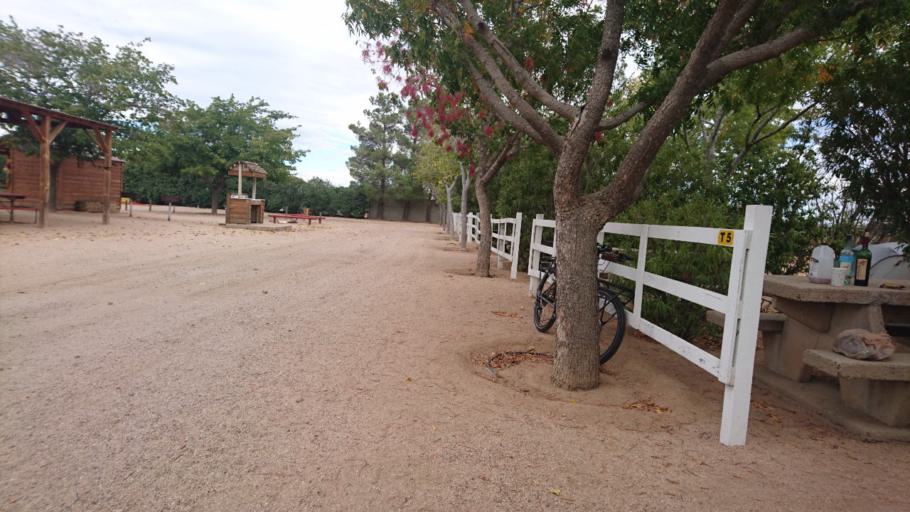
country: US
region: Arizona
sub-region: Mohave County
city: New Kingman-Butler
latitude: 35.2352
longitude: -114.0175
